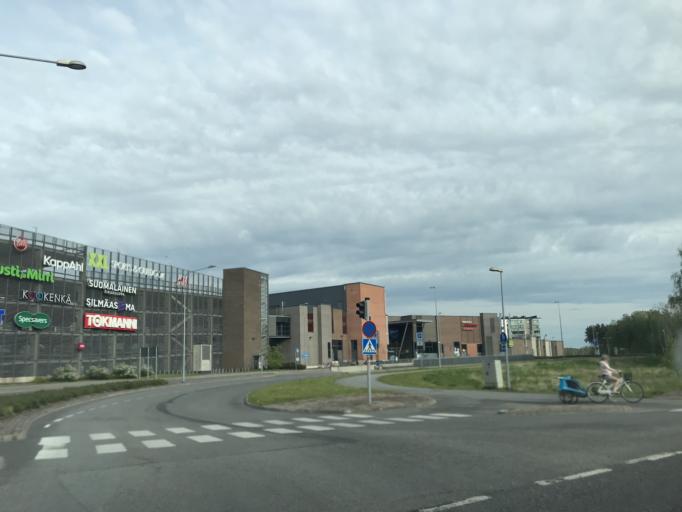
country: FI
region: Varsinais-Suomi
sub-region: Turku
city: Turku
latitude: 60.4304
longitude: 22.3178
